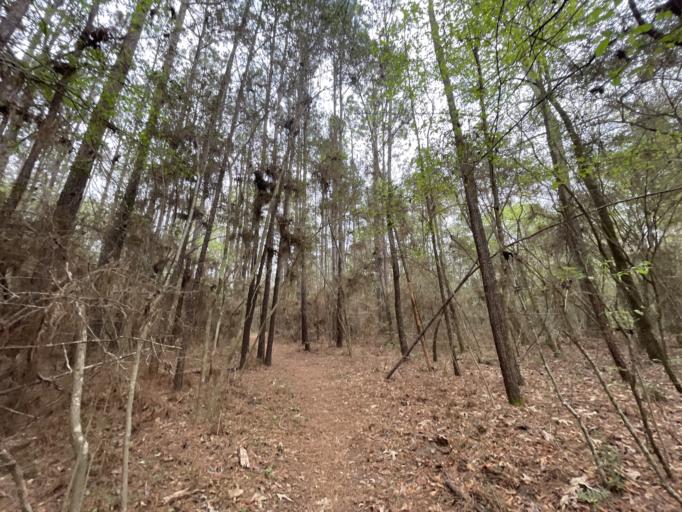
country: US
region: Texas
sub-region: Walker County
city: Huntsville
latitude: 30.6610
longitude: -95.4936
